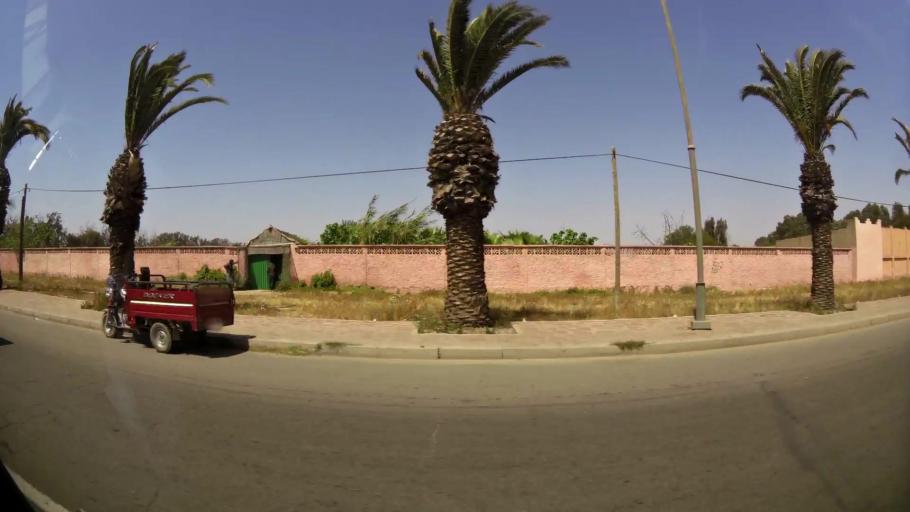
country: MA
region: Souss-Massa-Draa
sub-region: Inezgane-Ait Mellou
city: Inezgane
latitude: 30.3555
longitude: -9.5139
